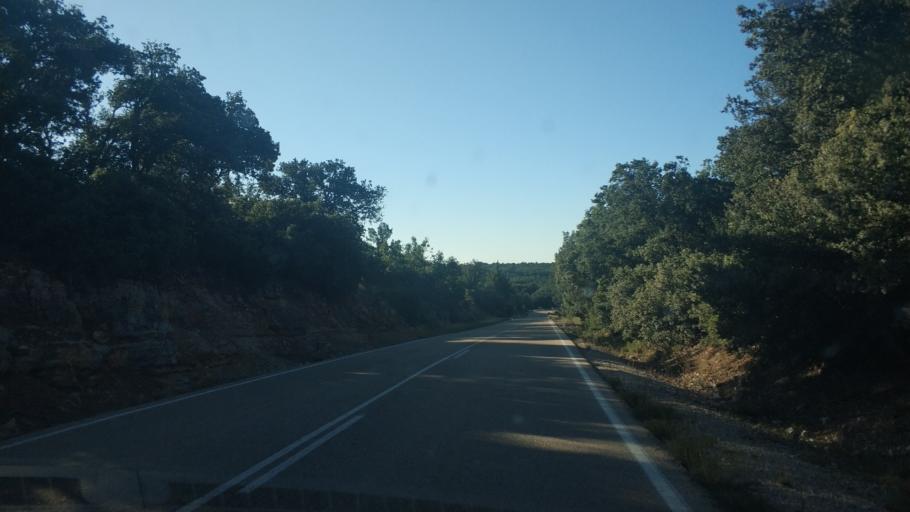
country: ES
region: Castille and Leon
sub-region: Provincia de Soria
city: Montejo de Tiermes
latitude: 41.4146
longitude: -3.2028
